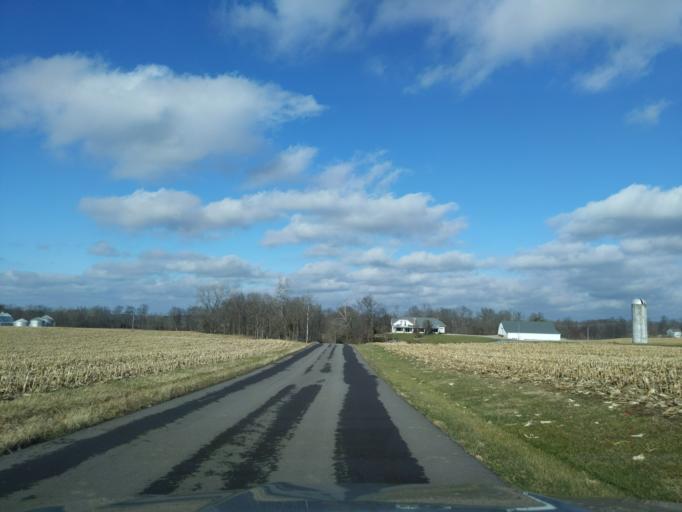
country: US
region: Indiana
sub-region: Decatur County
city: Greensburg
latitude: 39.2717
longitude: -85.4839
